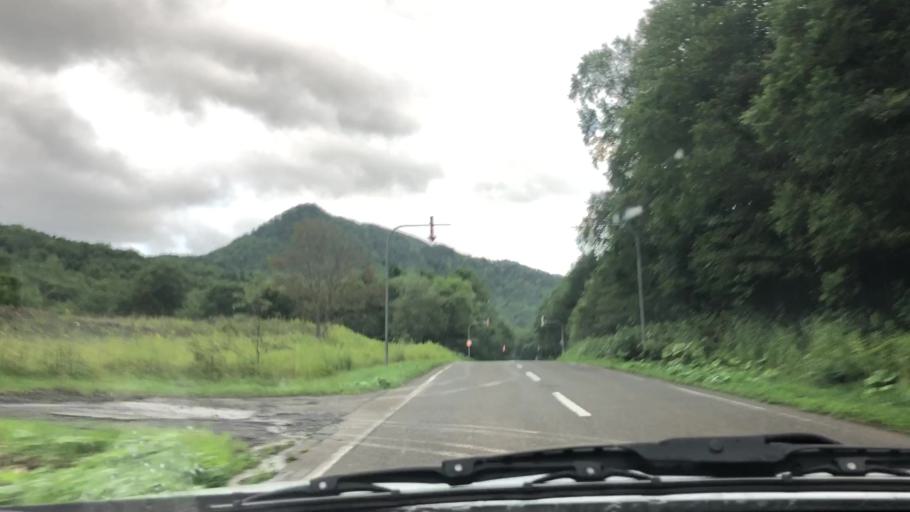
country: JP
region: Hokkaido
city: Shimo-furano
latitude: 42.9243
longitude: 142.3746
